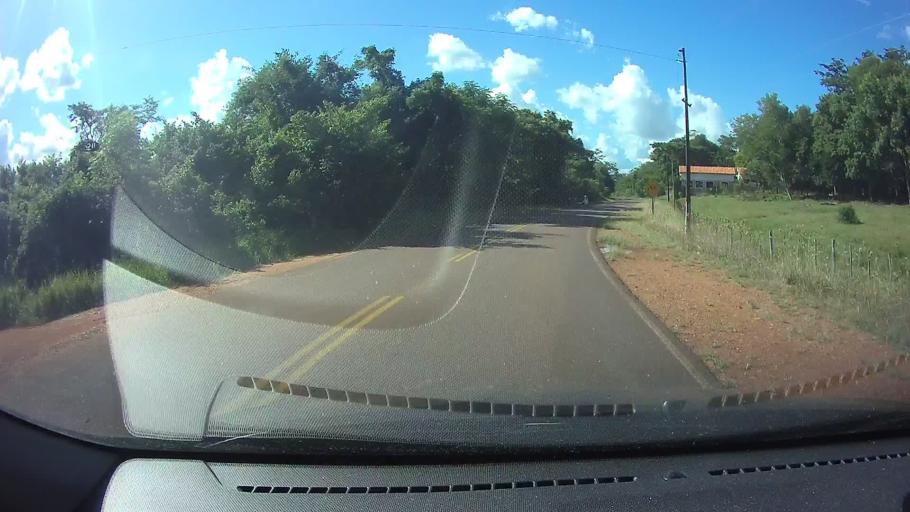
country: PY
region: Paraguari
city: Sapucai
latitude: -25.6501
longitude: -56.8630
